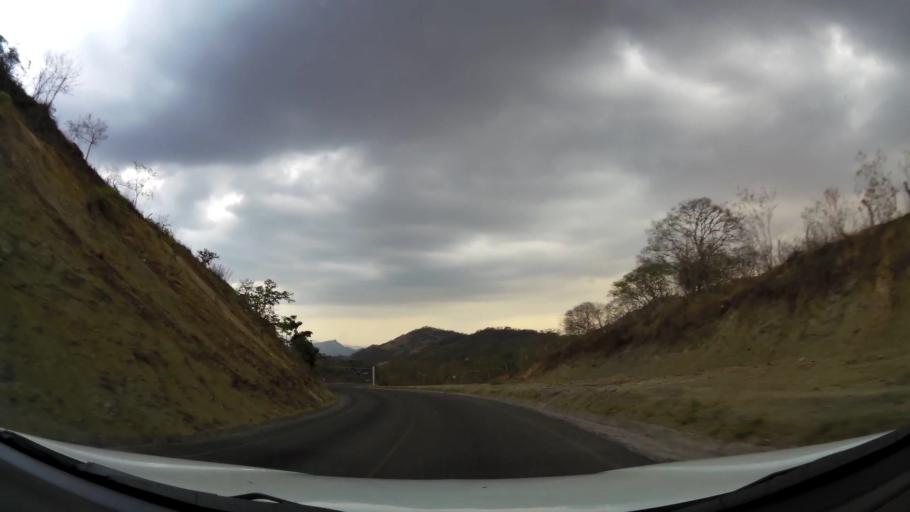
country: NI
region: Jinotega
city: Jinotega
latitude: 12.9972
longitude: -86.0284
